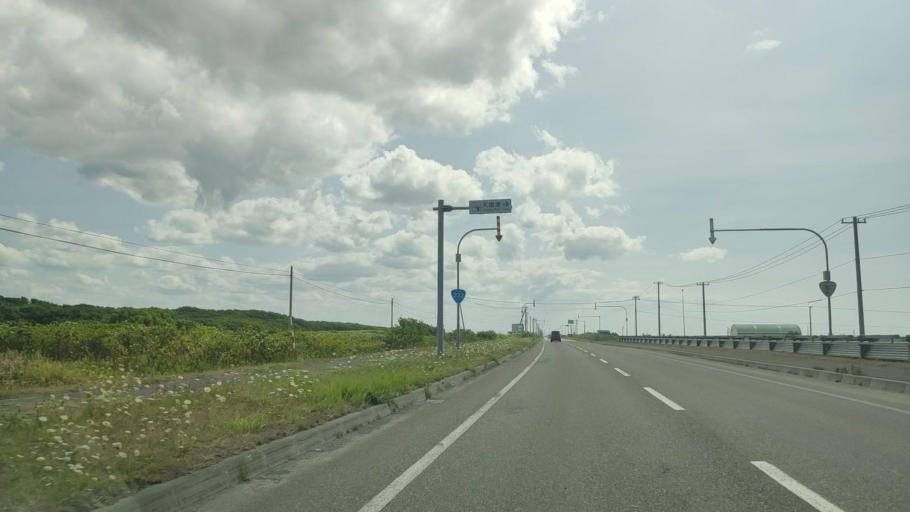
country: JP
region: Hokkaido
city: Makubetsu
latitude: 44.8687
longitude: 141.7526
